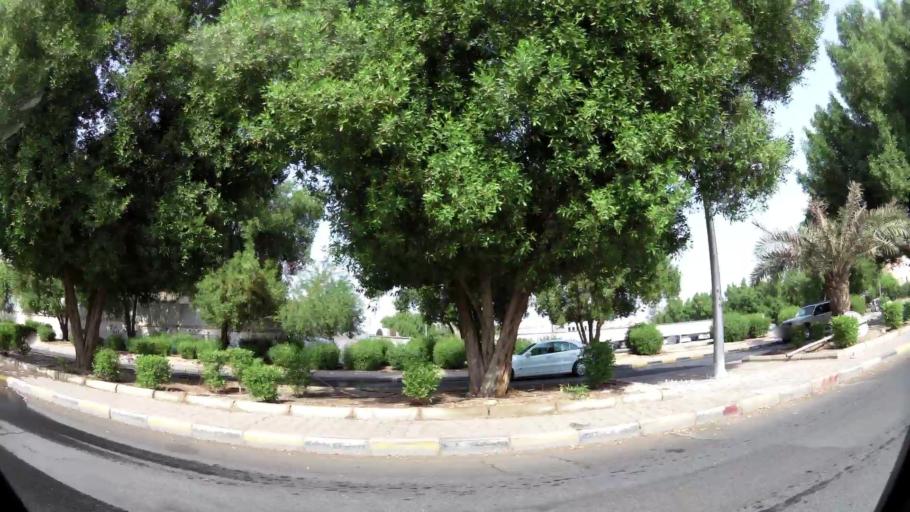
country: KW
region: Muhafazat al Jahra'
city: Al Jahra'
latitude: 29.3266
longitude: 47.6548
